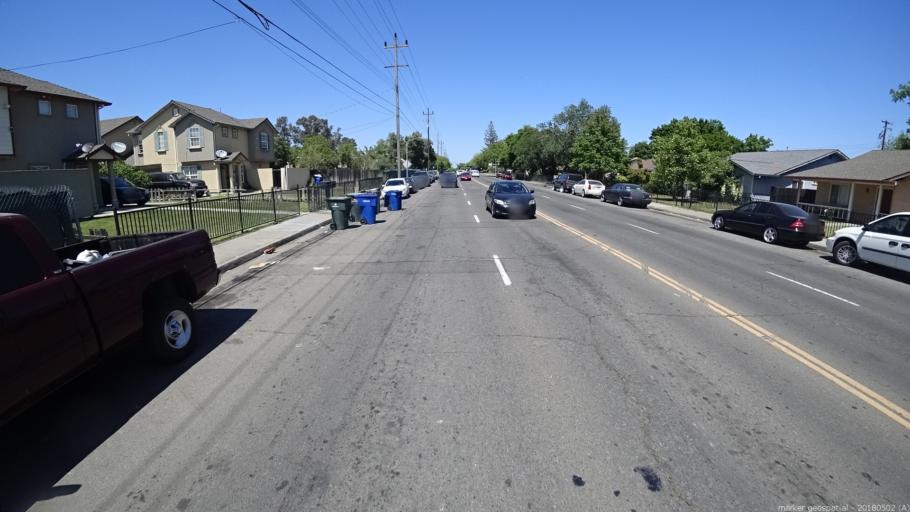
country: US
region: California
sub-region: Sacramento County
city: Rio Linda
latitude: 38.6338
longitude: -121.4461
